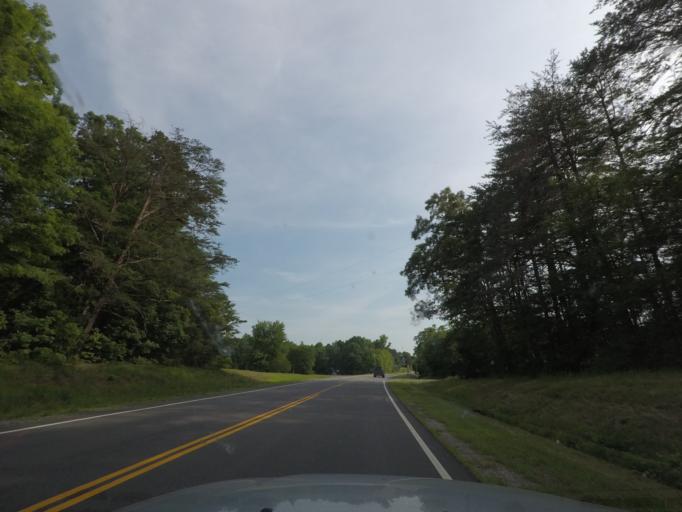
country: US
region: Virginia
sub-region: Mecklenburg County
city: Clarksville
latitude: 36.7556
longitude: -78.6312
